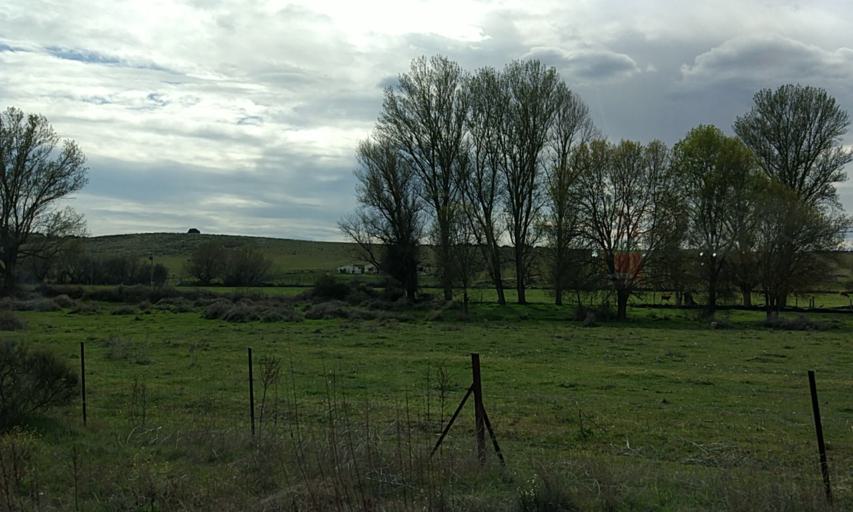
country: ES
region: Castille and Leon
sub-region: Provincia de Salamanca
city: Pastores
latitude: 40.5273
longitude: -6.5668
